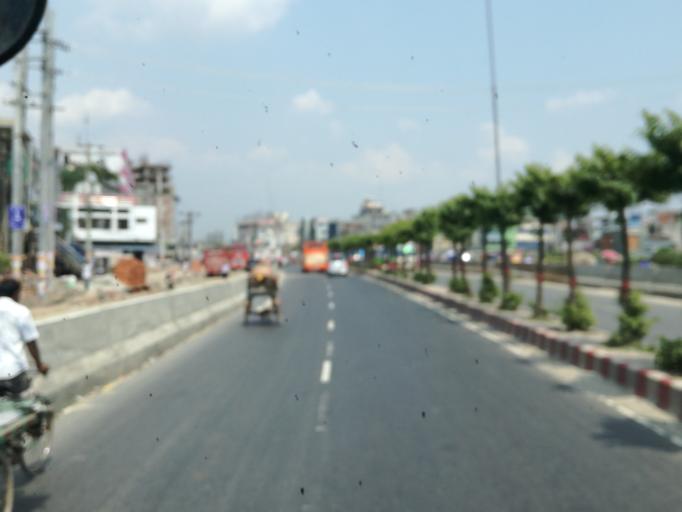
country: BD
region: Dhaka
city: Azimpur
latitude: 23.7935
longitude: 90.2695
